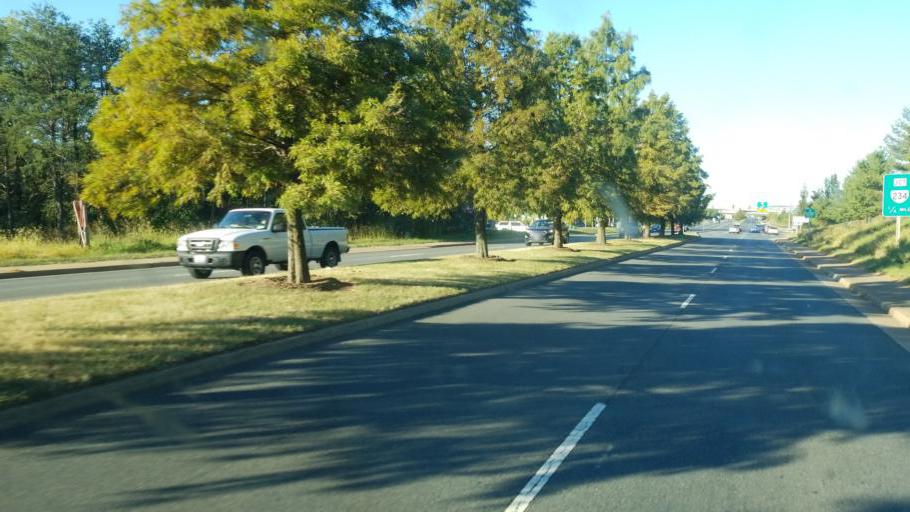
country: US
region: Virginia
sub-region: City of Manassas
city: Manassas
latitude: 38.7450
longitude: -77.5105
